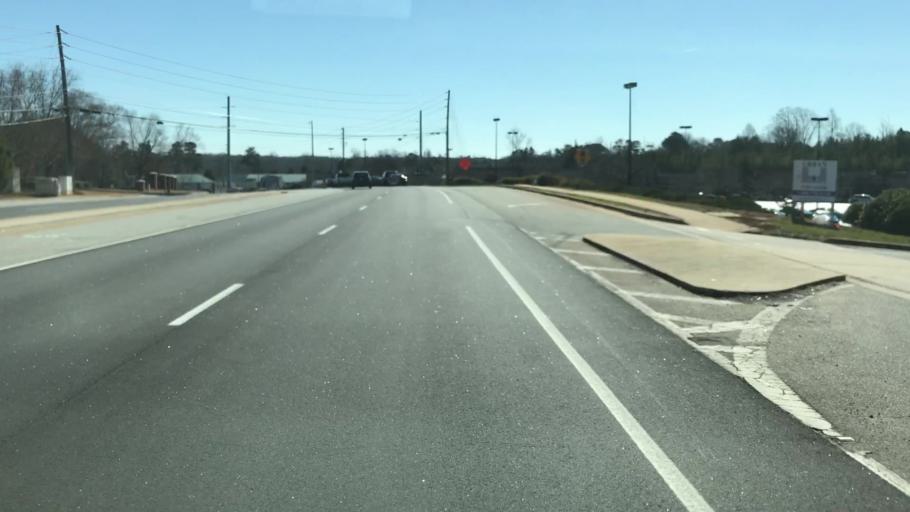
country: US
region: Georgia
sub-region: Gwinnett County
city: Lawrenceville
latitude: 33.9226
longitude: -84.0173
